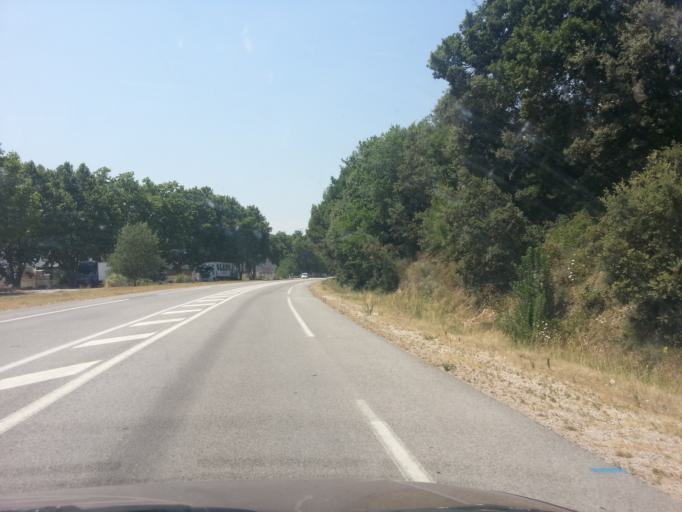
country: FR
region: Provence-Alpes-Cote d'Azur
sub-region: Departement du Var
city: Flassans-sur-Issole
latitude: 43.3694
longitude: 6.2096
